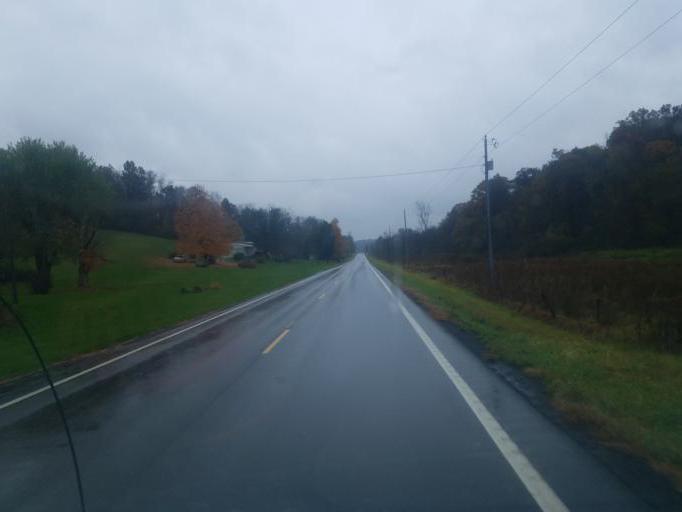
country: US
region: Ohio
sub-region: Muskingum County
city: Frazeysburg
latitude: 40.1895
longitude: -82.2304
